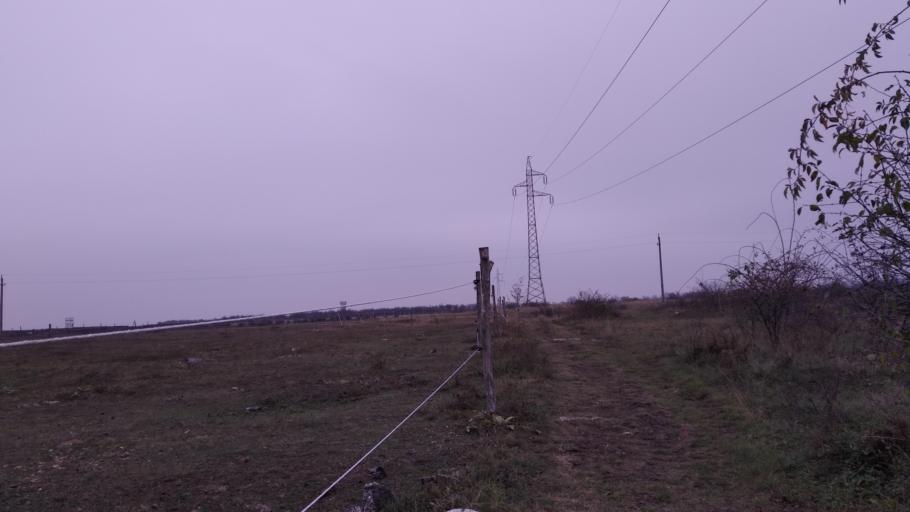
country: HU
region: Pest
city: Nagykovacsi
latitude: 47.6413
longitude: 19.0053
